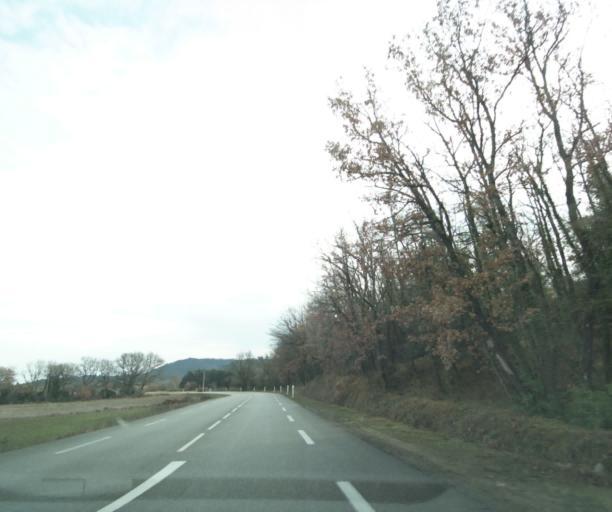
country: FR
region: Provence-Alpes-Cote d'Azur
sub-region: Departement du Var
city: Rougiers
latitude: 43.3948
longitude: 5.8656
